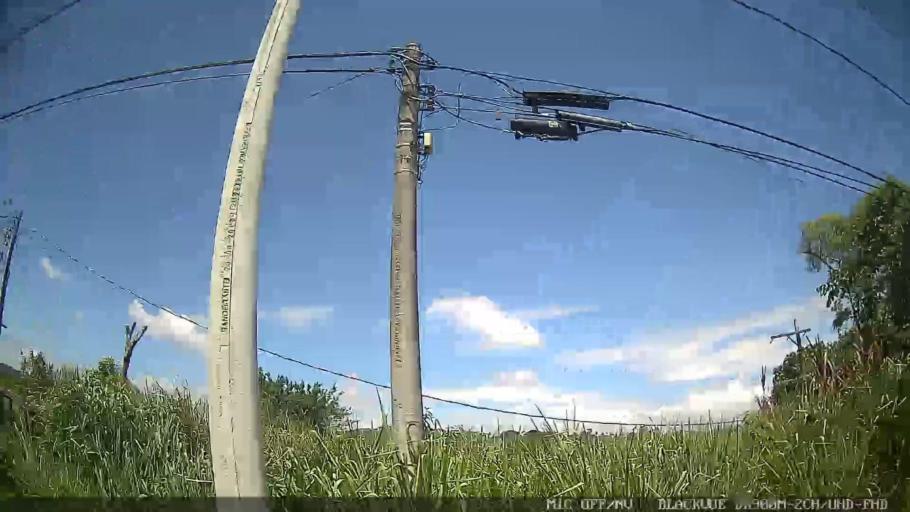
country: BR
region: Sao Paulo
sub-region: Biritiba-Mirim
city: Biritiba Mirim
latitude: -23.5718
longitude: -46.0827
